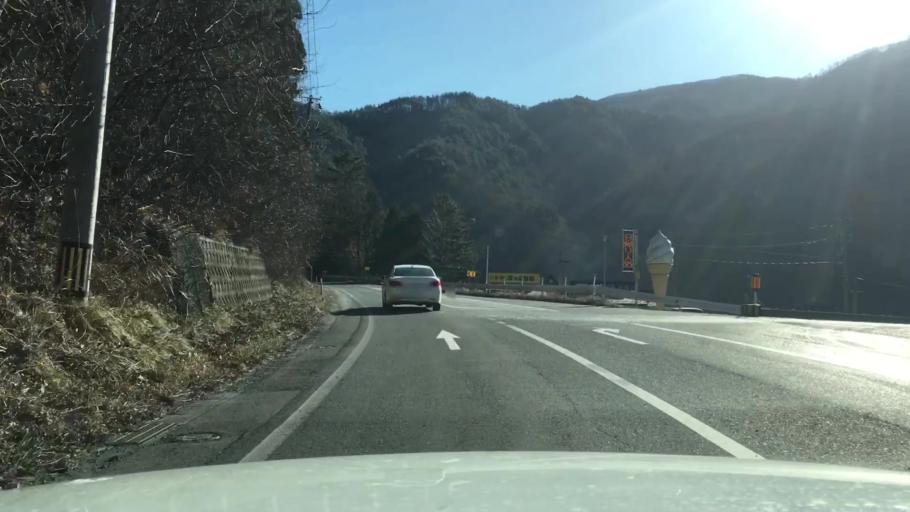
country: JP
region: Iwate
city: Miyako
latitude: 39.6162
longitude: 141.7965
